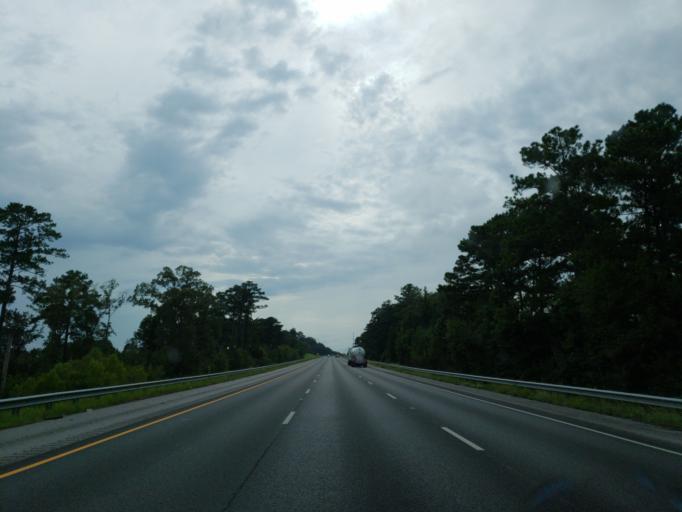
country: US
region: Alabama
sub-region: Tuscaloosa County
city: Vance
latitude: 33.1920
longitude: -87.2566
